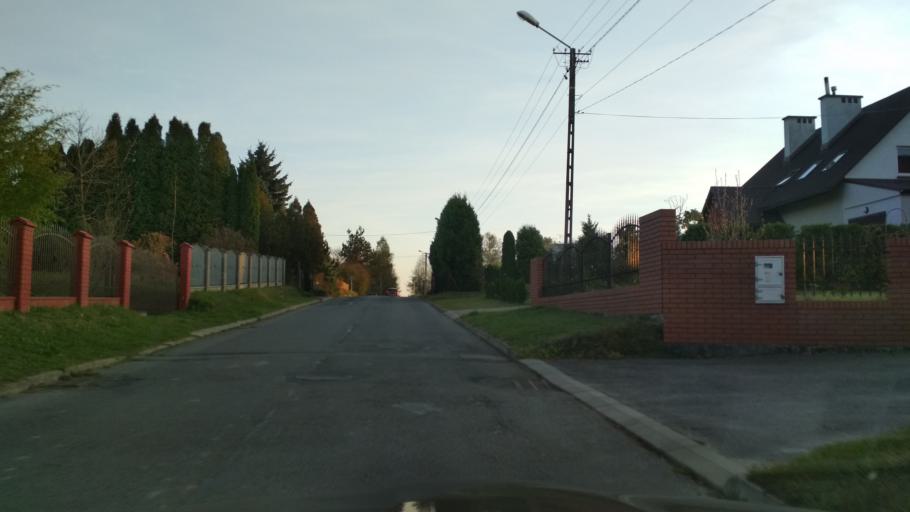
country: PL
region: Subcarpathian Voivodeship
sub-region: Powiat ropczycko-sedziszowski
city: Sedziszow Malopolski
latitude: 50.0642
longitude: 21.7113
